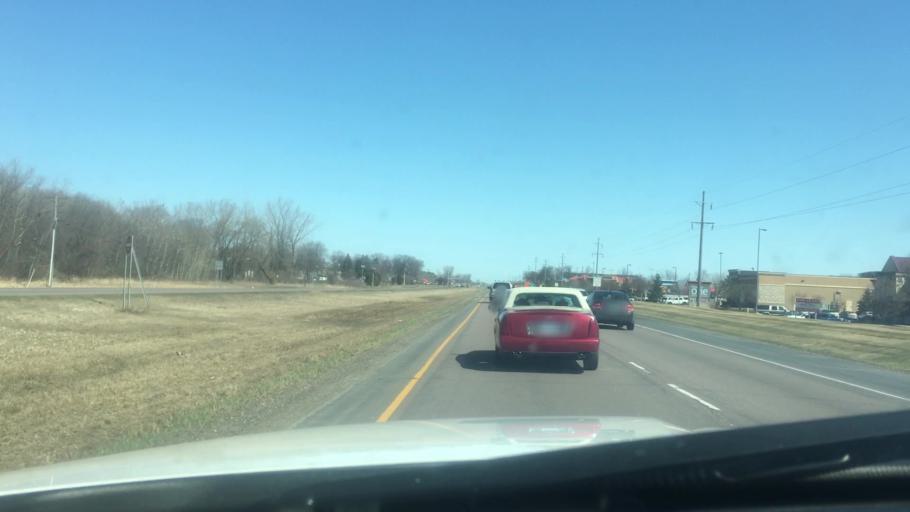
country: US
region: Minnesota
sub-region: Anoka County
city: Blaine
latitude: 45.1545
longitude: -93.2350
